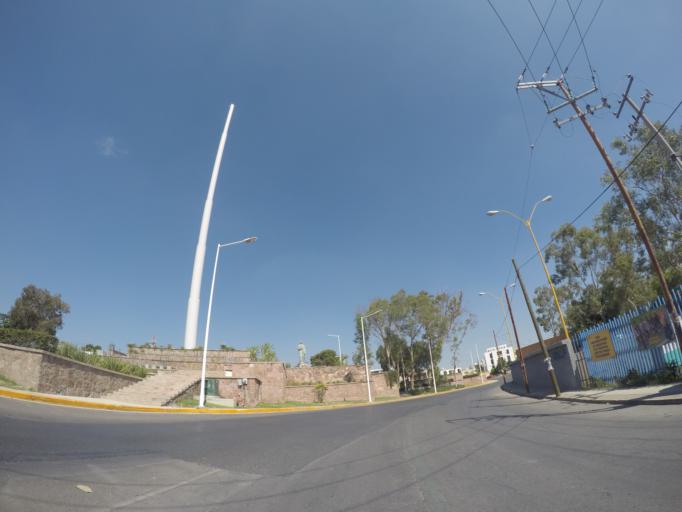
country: MX
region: San Luis Potosi
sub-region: San Luis Potosi
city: San Luis Potosi
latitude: 22.1428
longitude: -101.0173
